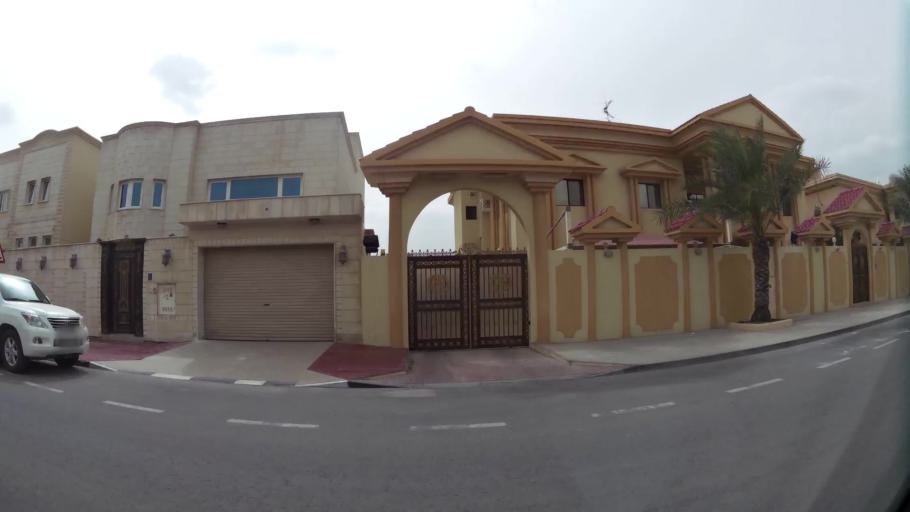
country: QA
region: Baladiyat ad Dawhah
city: Doha
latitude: 25.2487
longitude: 51.5280
